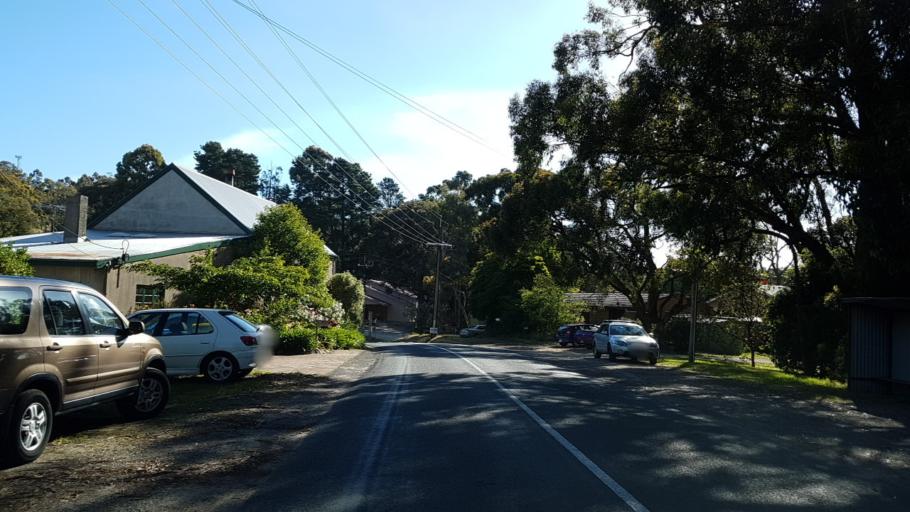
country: AU
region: South Australia
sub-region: Adelaide Hills
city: Adelaide Hills
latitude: -34.9394
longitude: 138.7381
